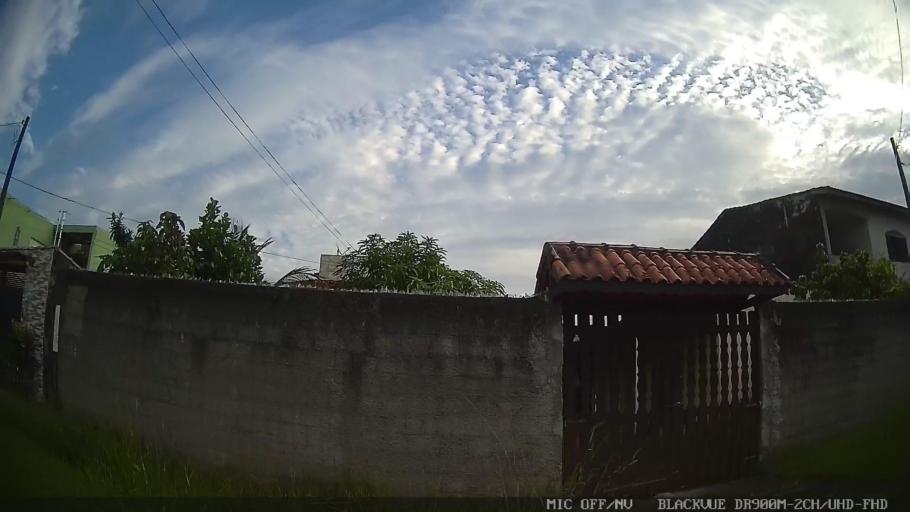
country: BR
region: Sao Paulo
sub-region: Itanhaem
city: Itanhaem
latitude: -24.1620
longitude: -46.7796
